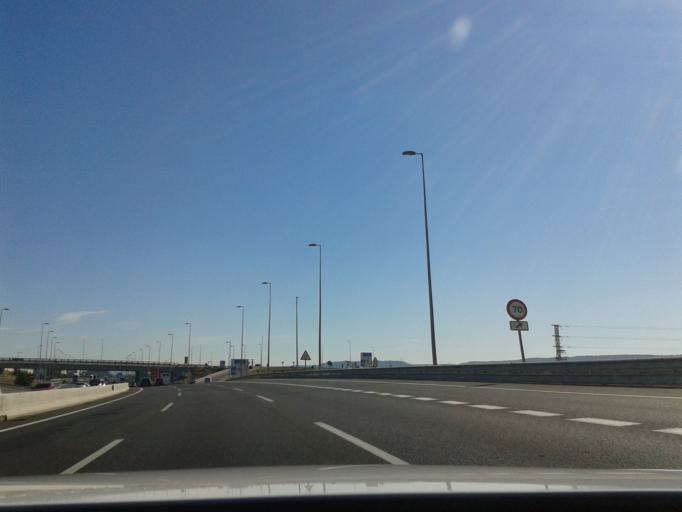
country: ES
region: Madrid
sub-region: Provincia de Madrid
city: Meco
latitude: 40.5290
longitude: -3.2926
